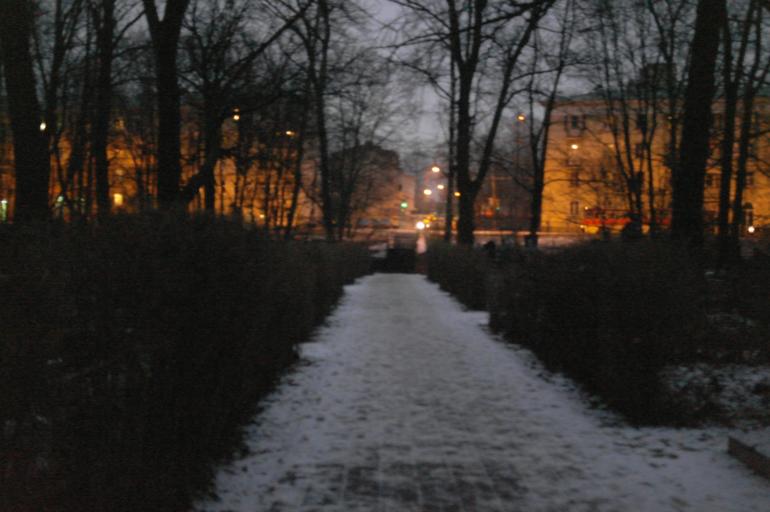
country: RU
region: St.-Petersburg
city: Centralniy
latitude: 59.8998
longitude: 30.3584
